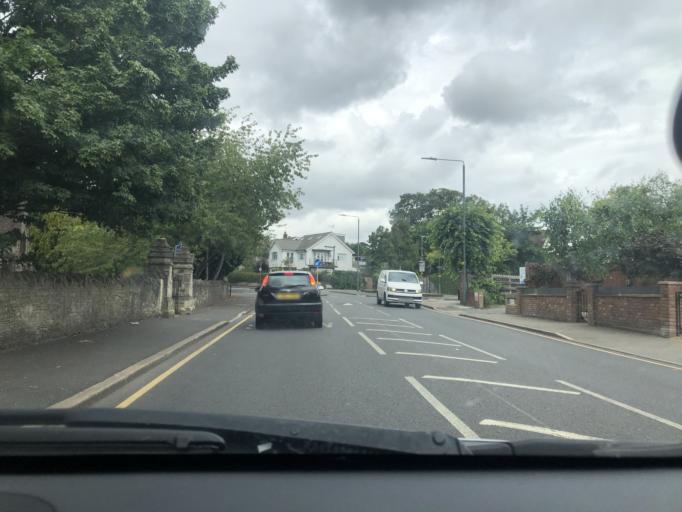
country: GB
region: England
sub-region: Greater London
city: Bexley
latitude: 51.4424
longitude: 0.1445
